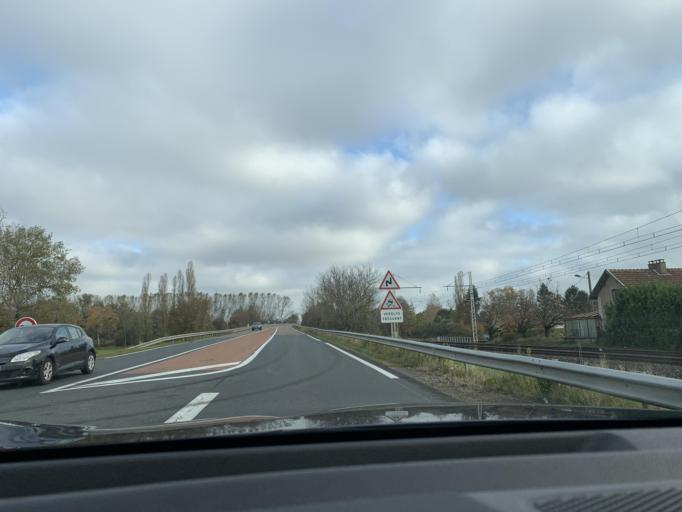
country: FR
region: Bourgogne
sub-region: Departement de Saone-et-Loire
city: Saint-Martin-Belle-Roche
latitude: 46.3728
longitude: 4.8587
